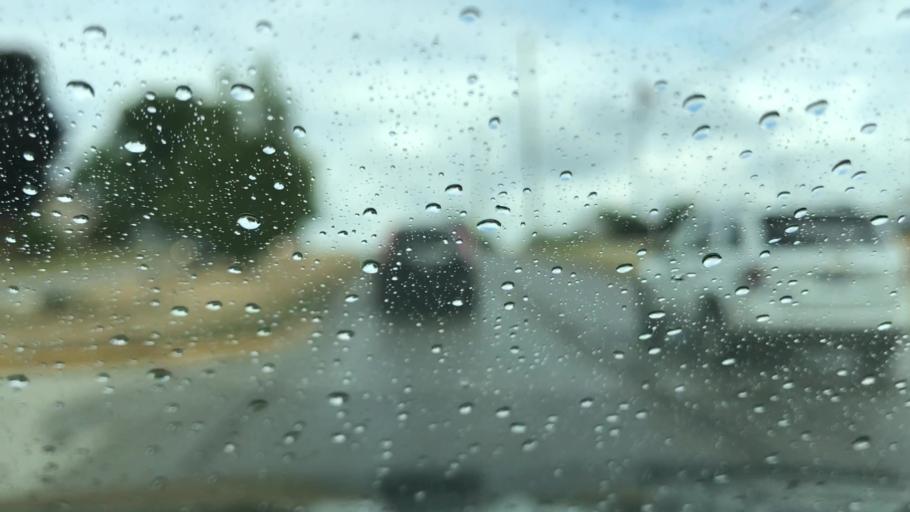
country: US
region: Michigan
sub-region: Kent County
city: Wyoming
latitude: 42.8842
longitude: -85.6936
